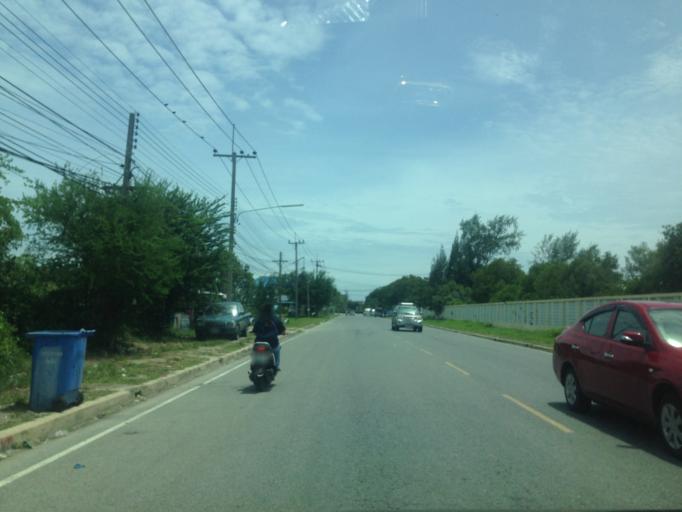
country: TH
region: Chon Buri
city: Chon Buri
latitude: 13.3436
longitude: 100.9520
